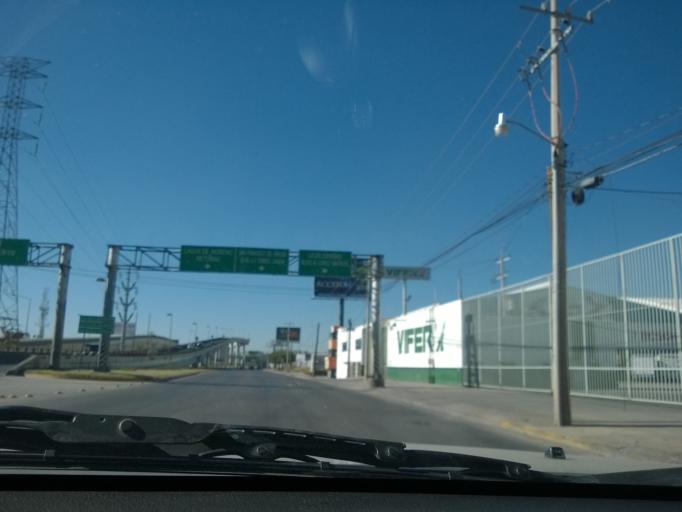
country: MX
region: Guanajuato
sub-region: Leon
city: Fraccionamiento Paraiso Real
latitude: 21.1006
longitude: -101.6251
